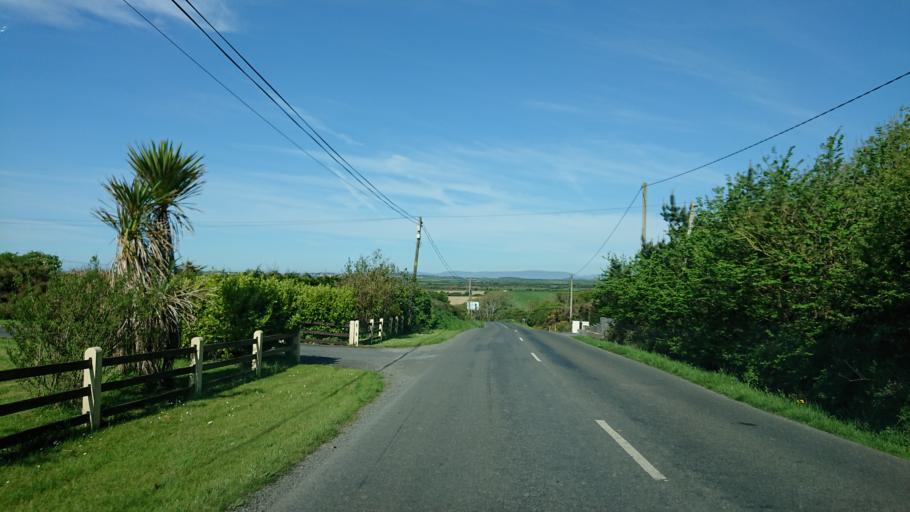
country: IE
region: Munster
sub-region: Waterford
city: Dunmore East
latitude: 52.1703
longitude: -7.0656
